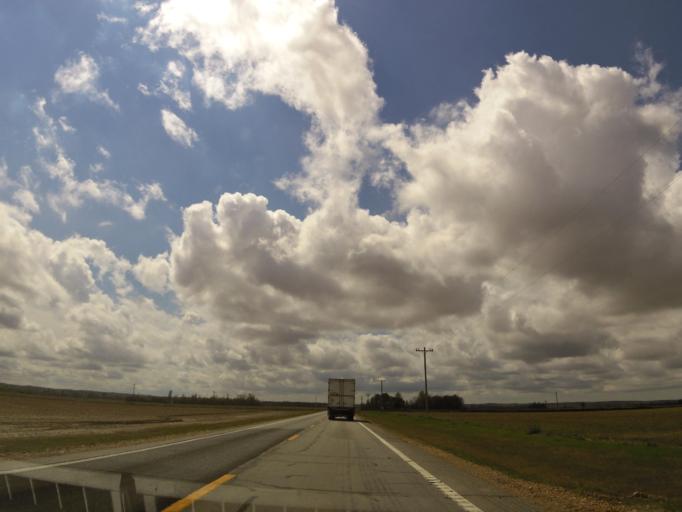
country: US
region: Arkansas
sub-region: Clay County
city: Corning
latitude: 36.2712
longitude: -90.5349
